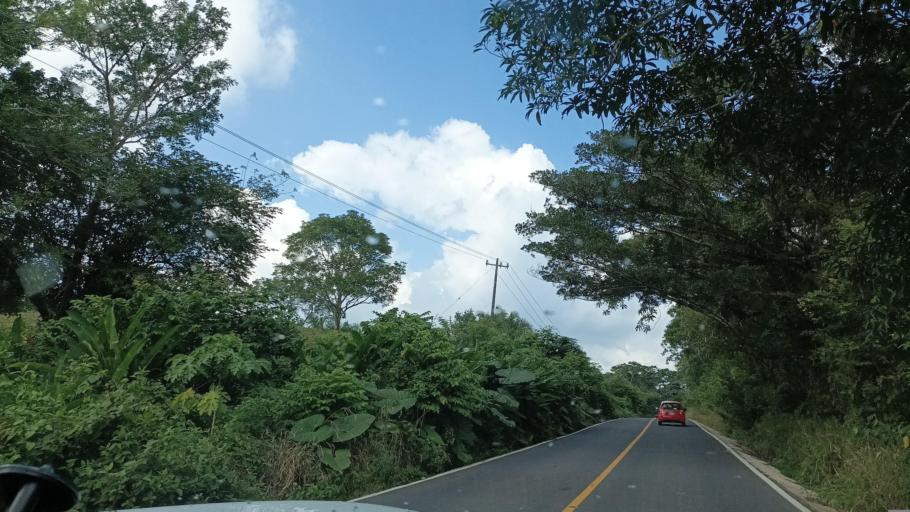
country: MX
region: Tabasco
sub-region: Huimanguillo
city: Francisco Rueda
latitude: 17.7367
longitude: -94.1063
